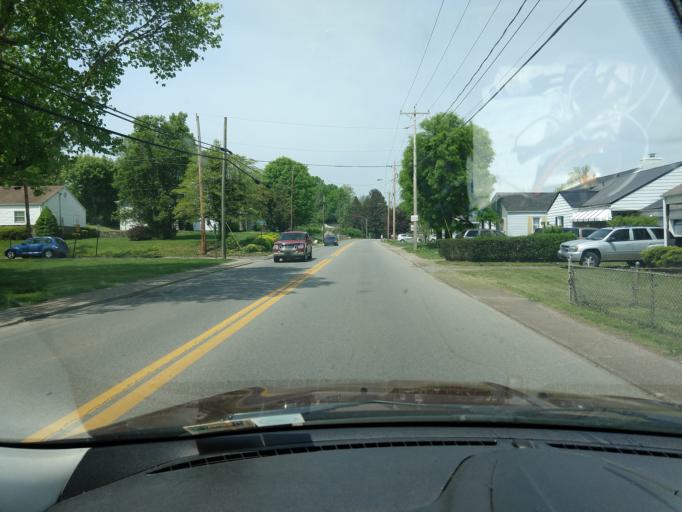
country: US
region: West Virginia
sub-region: Kanawha County
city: Saint Albans
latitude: 38.3782
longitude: -81.8166
